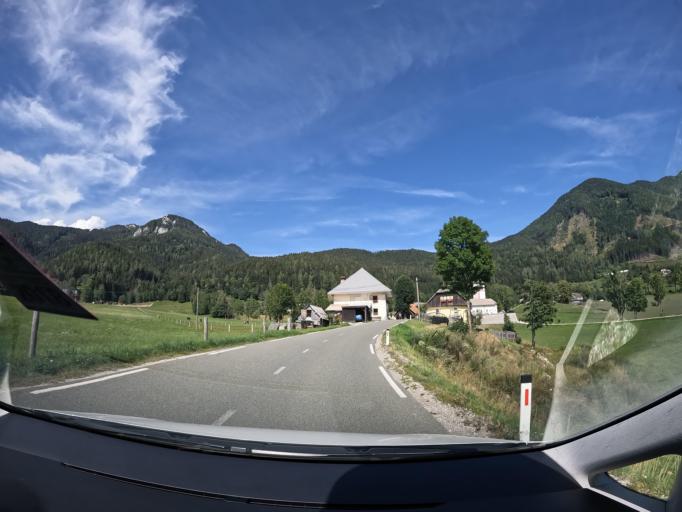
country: AT
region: Carinthia
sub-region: Politischer Bezirk Feldkirchen
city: Feldkirchen in Karnten
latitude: 46.7355
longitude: 14.1483
